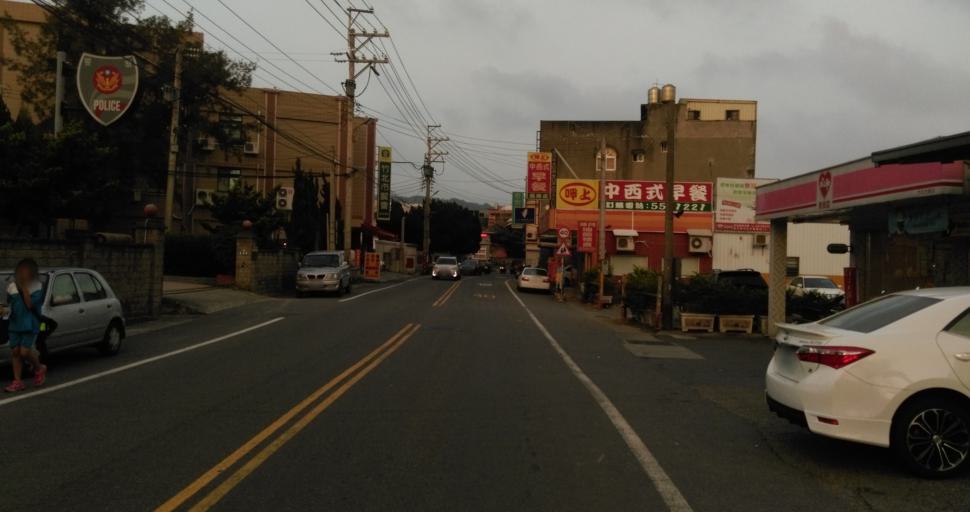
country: TW
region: Taiwan
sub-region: Hsinchu
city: Zhubei
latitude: 24.8609
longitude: 120.9633
